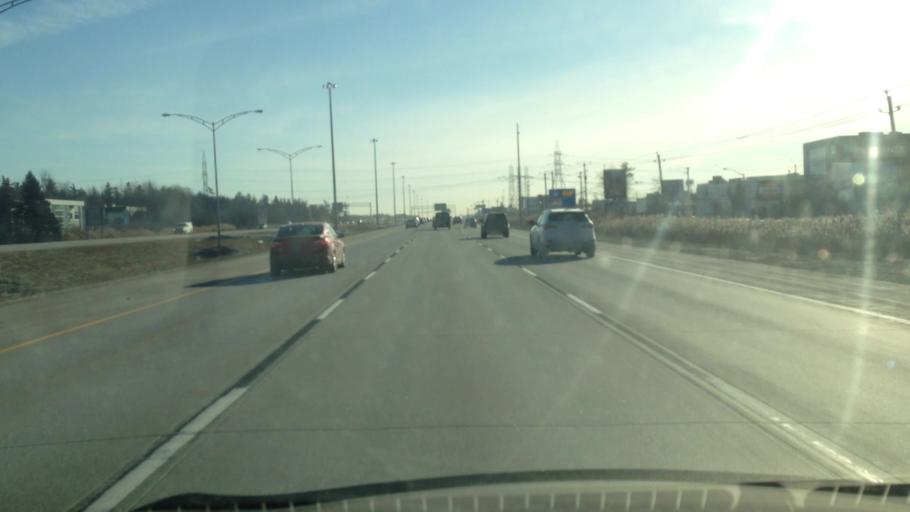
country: CA
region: Quebec
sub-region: Laurentides
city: Blainville
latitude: 45.6858
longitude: -73.9273
